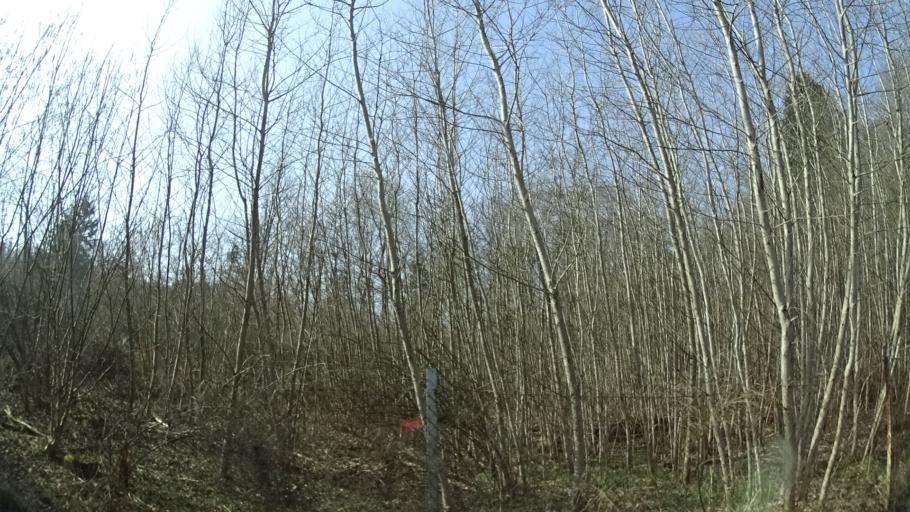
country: DE
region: Saarland
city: Nohfelden
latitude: 49.5864
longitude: 7.1197
